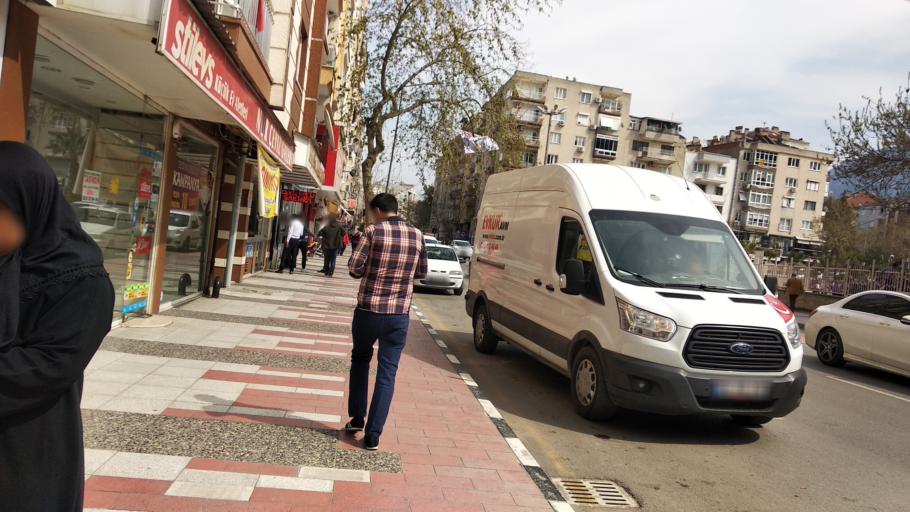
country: TR
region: Manisa
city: Manisa
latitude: 38.6139
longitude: 27.4207
